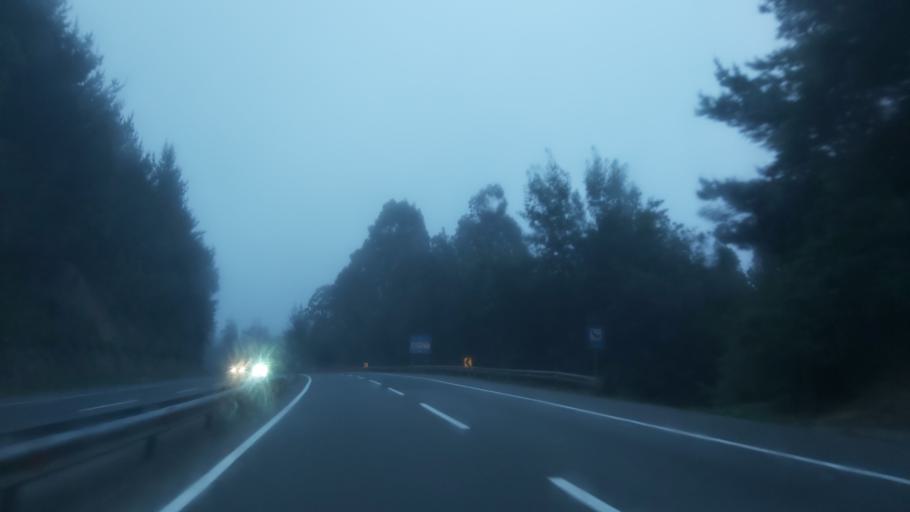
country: CL
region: Biobio
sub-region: Provincia de Concepcion
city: Penco
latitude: -36.7423
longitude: -72.9087
